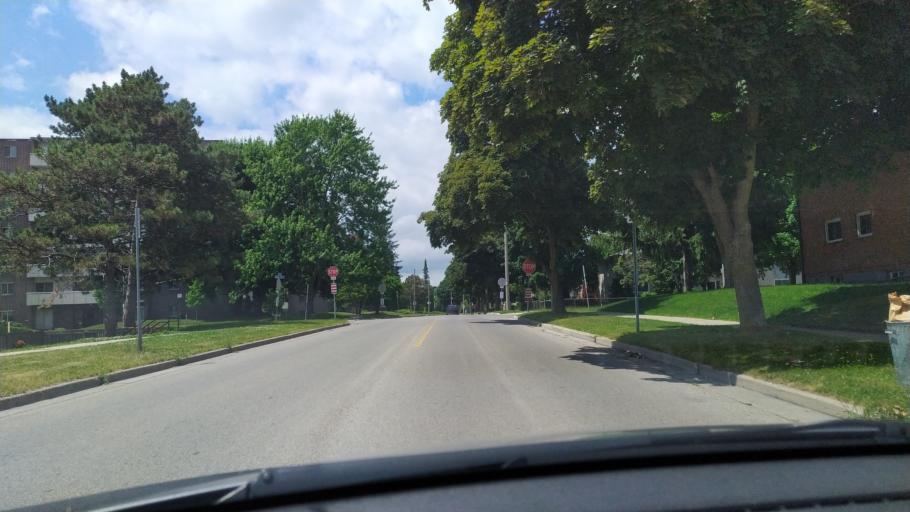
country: CA
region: Ontario
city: Kitchener
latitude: 43.4504
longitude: -80.4389
